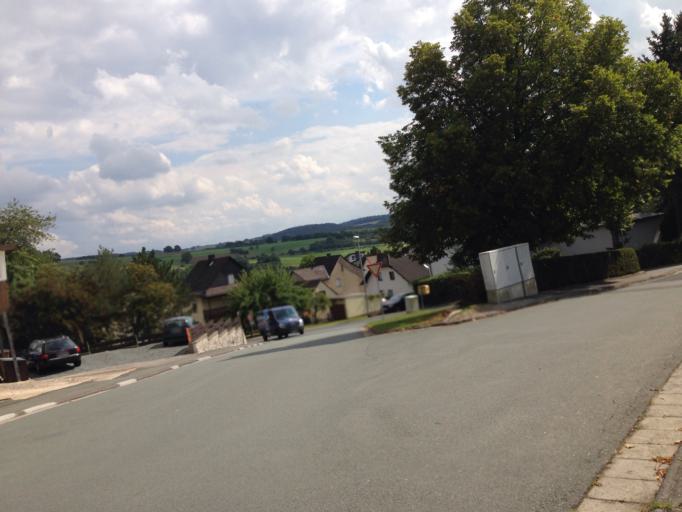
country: DE
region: Hesse
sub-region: Regierungsbezirk Giessen
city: Lohnberg
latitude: 50.5100
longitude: 8.2653
